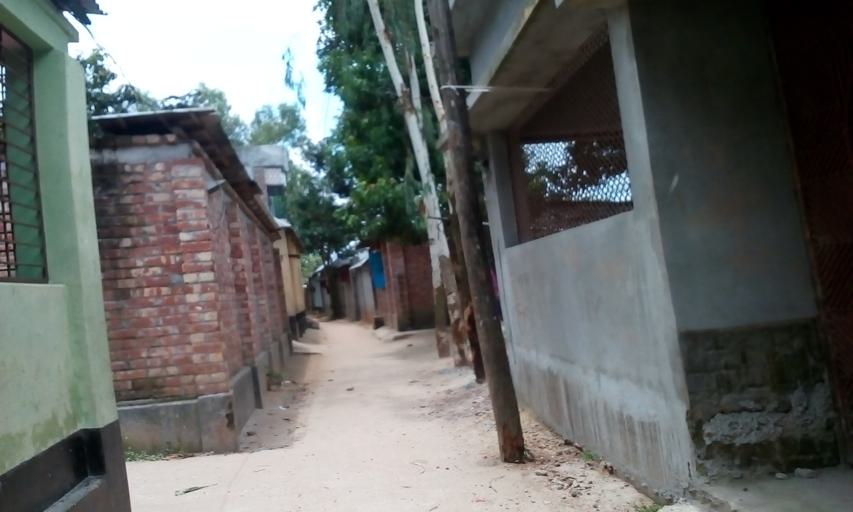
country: IN
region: West Bengal
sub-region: Dakshin Dinajpur
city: Balurghat
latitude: 25.3824
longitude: 88.9960
